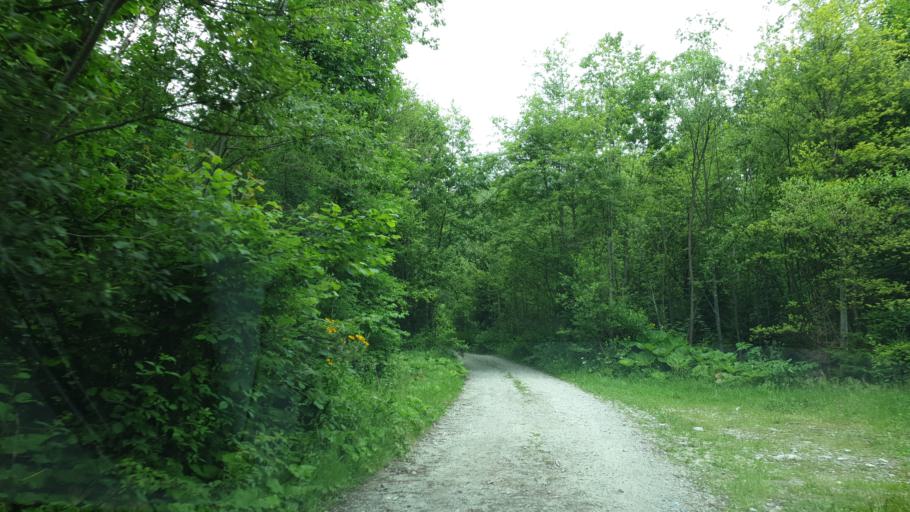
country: RO
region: Hunedoara
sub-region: Comuna Uricani
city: Uricani
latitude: 45.3066
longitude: 22.9863
